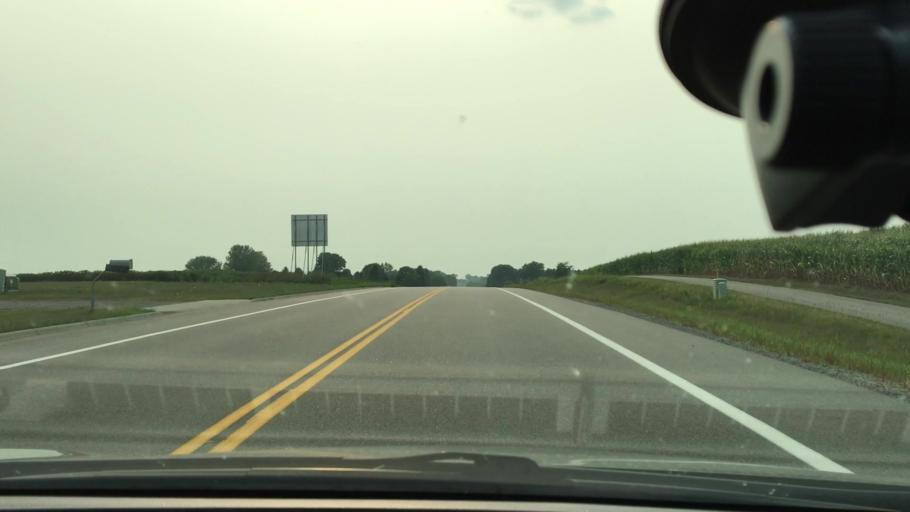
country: US
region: Minnesota
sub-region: Wright County
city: Otsego
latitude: 45.2526
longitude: -93.6041
